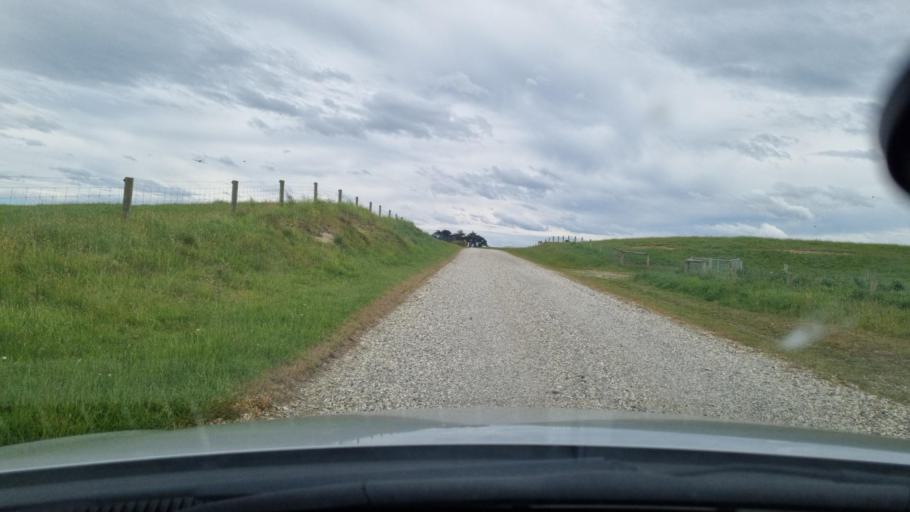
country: NZ
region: Southland
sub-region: Invercargill City
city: Invercargill
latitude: -46.3981
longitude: 168.2653
